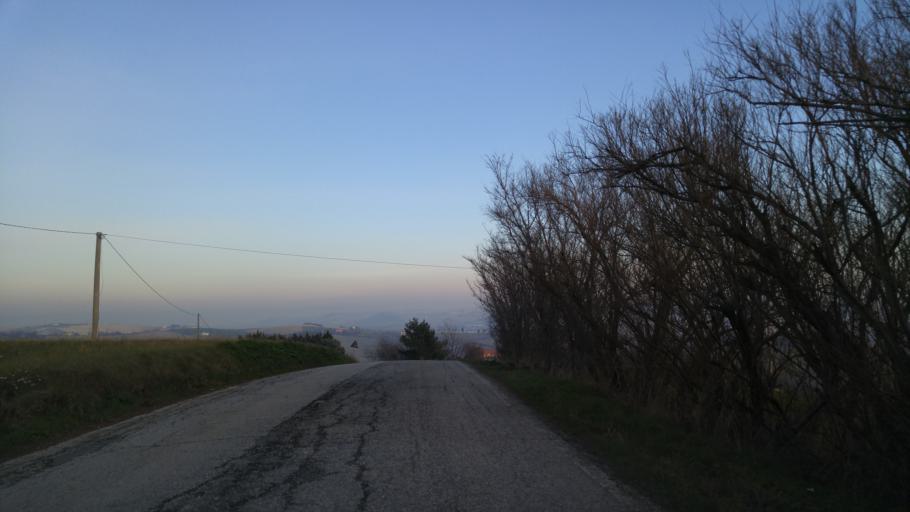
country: IT
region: The Marches
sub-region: Provincia di Pesaro e Urbino
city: Monte Porzio
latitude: 43.6974
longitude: 13.0218
